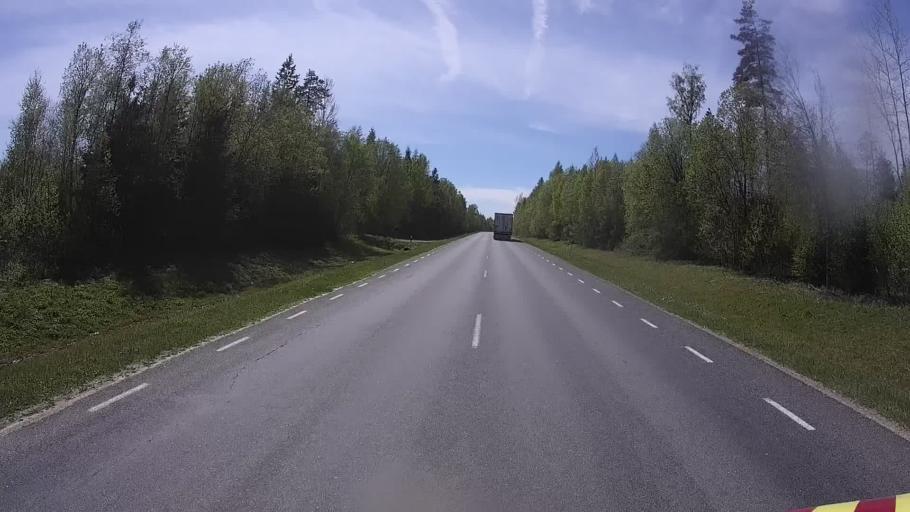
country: LV
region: Apes Novads
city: Ape
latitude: 57.7179
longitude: 26.7674
